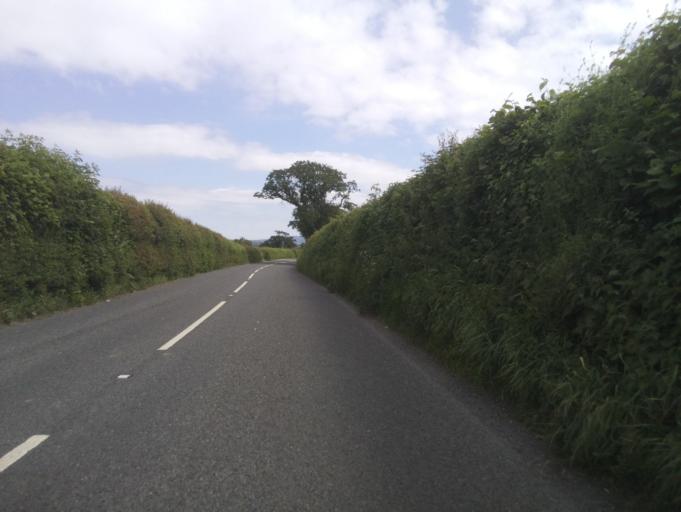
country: GB
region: England
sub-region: Somerset
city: Milborne Port
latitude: 51.0230
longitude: -2.4657
